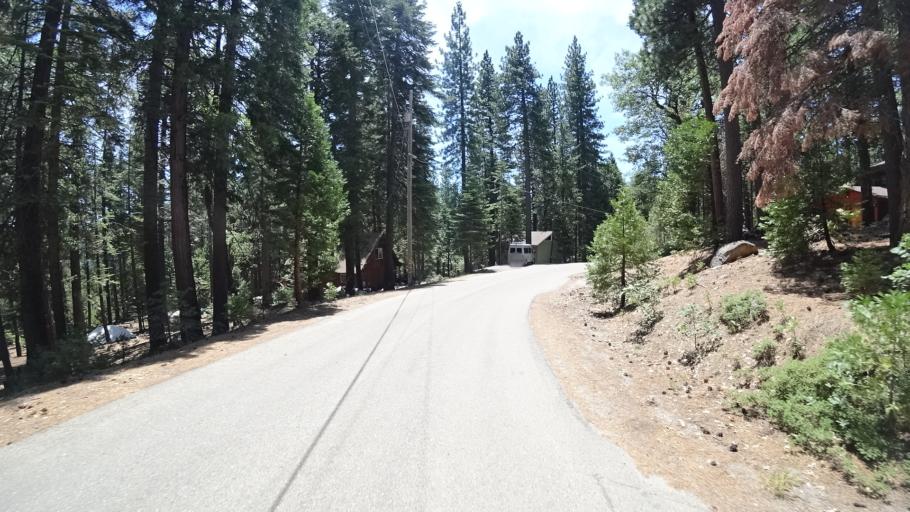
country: US
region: California
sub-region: Calaveras County
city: Arnold
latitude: 38.3121
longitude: -120.2542
